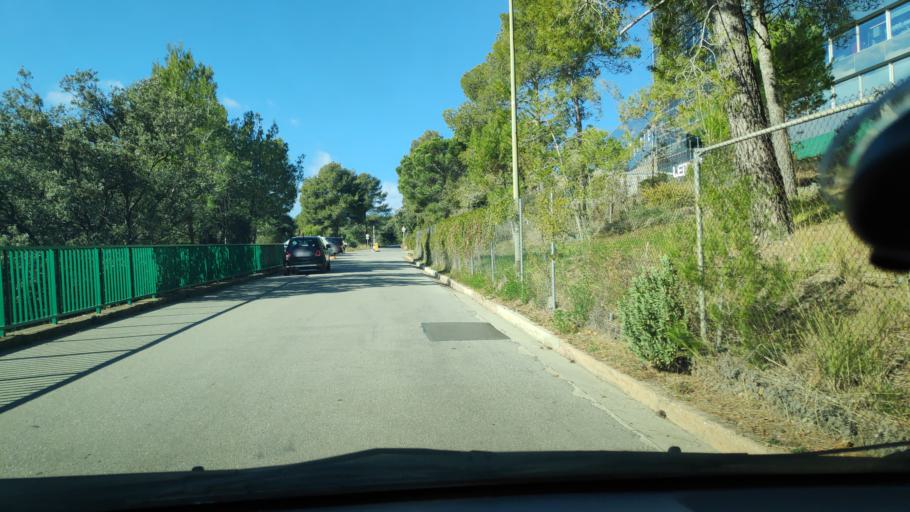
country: ES
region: Catalonia
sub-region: Provincia de Barcelona
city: Matadepera
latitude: 41.5976
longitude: 2.0111
